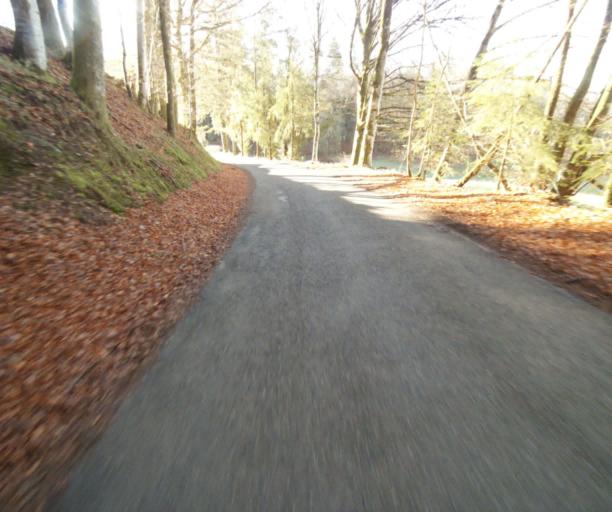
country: FR
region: Limousin
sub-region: Departement de la Correze
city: Laguenne
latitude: 45.2795
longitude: 1.8577
